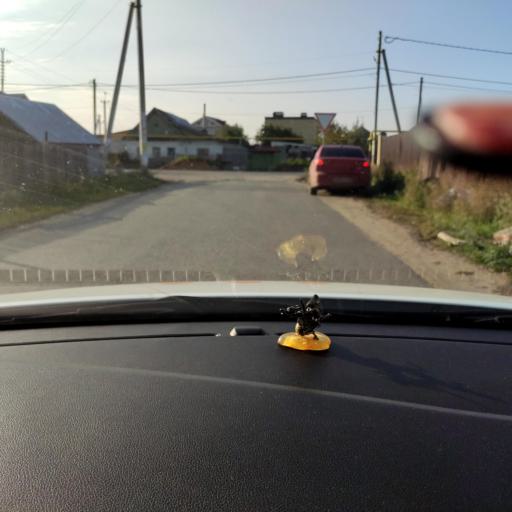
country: RU
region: Tatarstan
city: Staroye Arakchino
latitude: 55.8110
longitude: 48.9133
